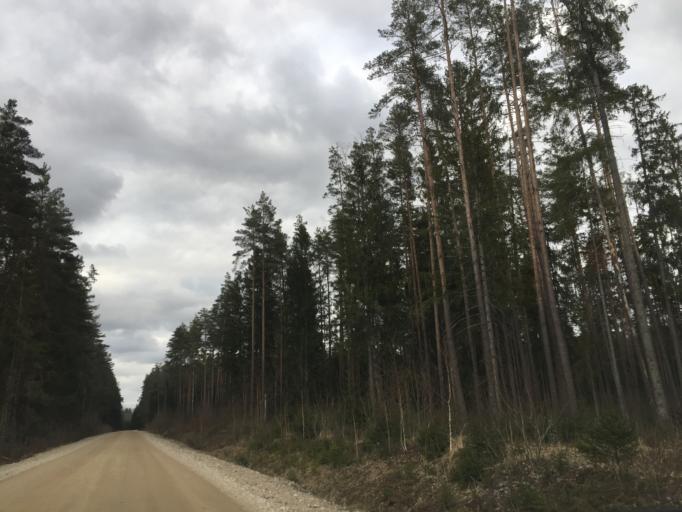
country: LV
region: Jaunjelgava
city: Jaunjelgava
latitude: 56.5900
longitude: 25.0408
